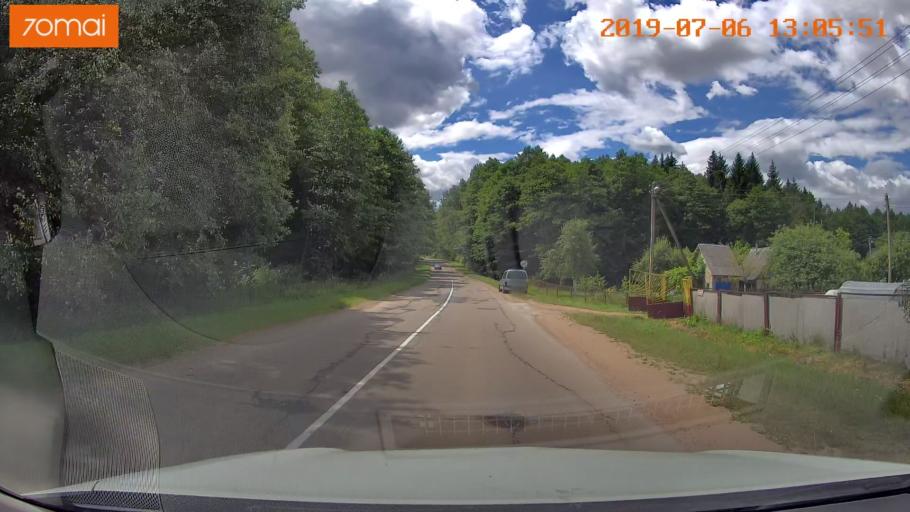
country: BY
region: Minsk
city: Dzyarzhynsk
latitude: 53.6860
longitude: 27.0611
